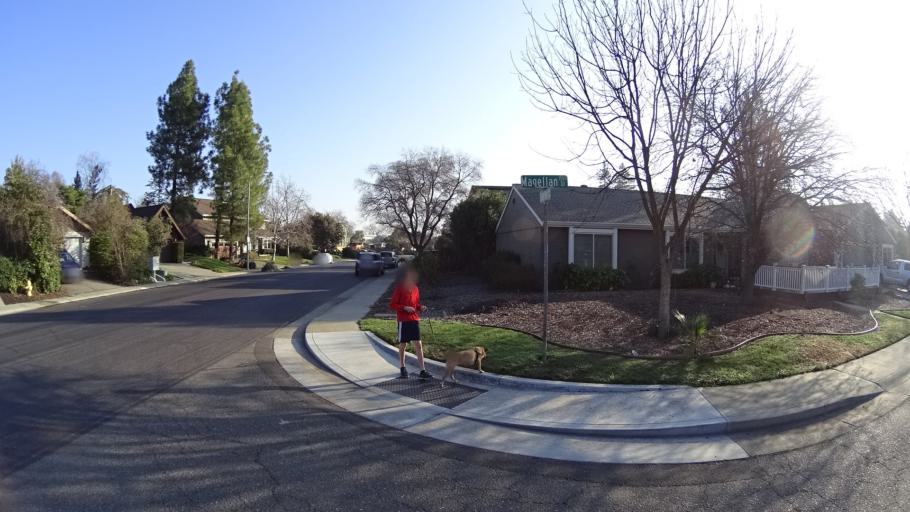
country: US
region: California
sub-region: Yolo County
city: Davis
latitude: 38.5577
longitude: -121.7919
